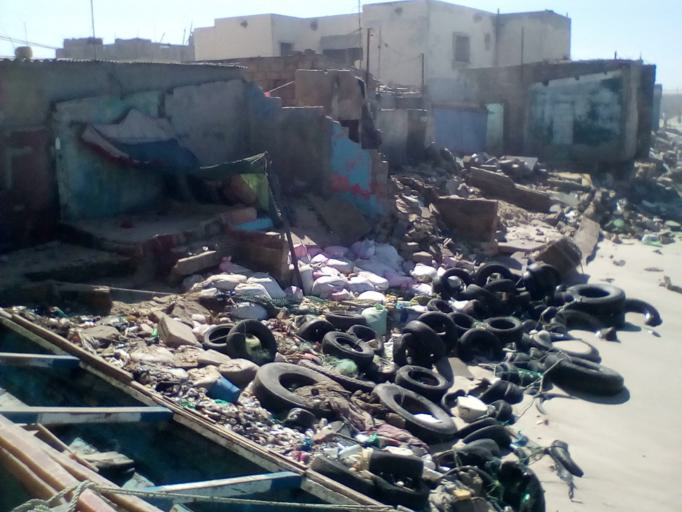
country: SN
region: Saint-Louis
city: Saint-Louis
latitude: 16.0196
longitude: -16.5095
